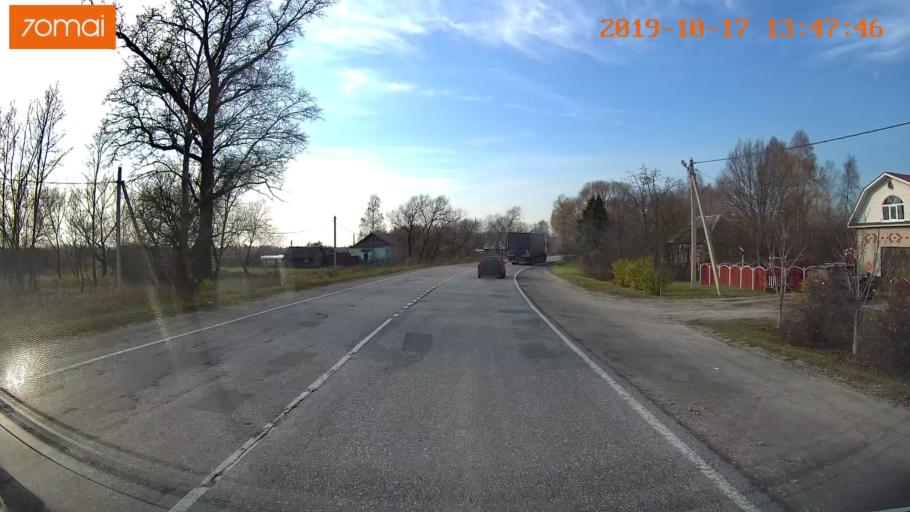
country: RU
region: Rjazan
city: Tuma
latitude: 55.1457
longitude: 40.4666
